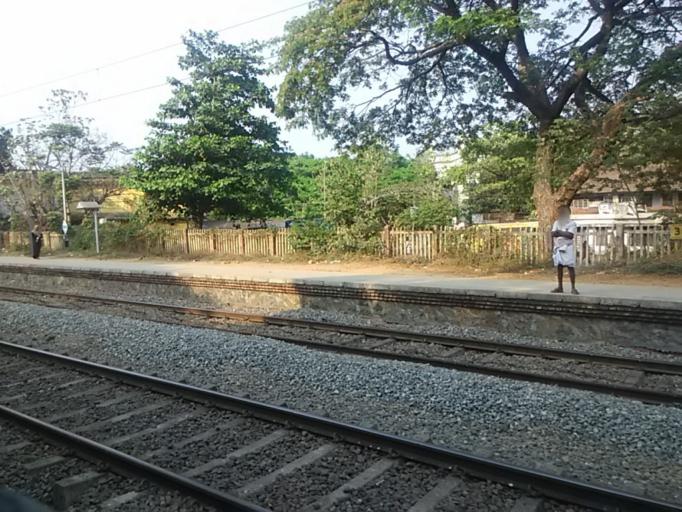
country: IN
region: Kerala
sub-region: Malappuram
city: Pariyapuram
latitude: 11.0480
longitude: 75.8599
